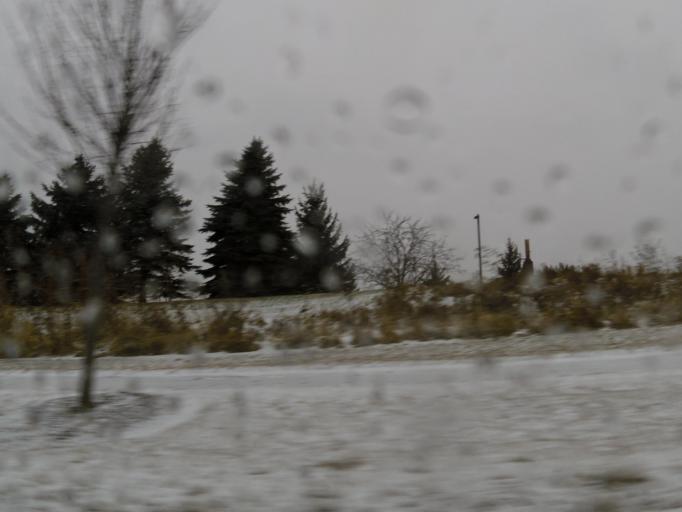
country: US
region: Minnesota
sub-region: Washington County
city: Oakdale
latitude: 44.9549
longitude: -92.9237
